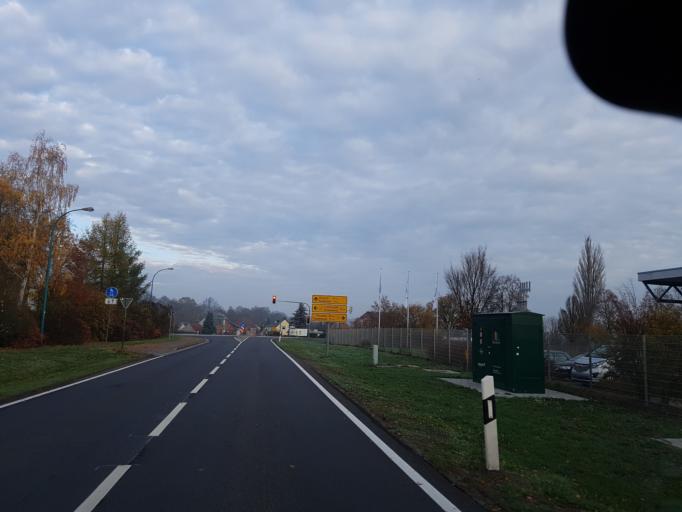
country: DE
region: Saxony-Anhalt
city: Kropstadt
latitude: 51.9588
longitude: 12.7470
